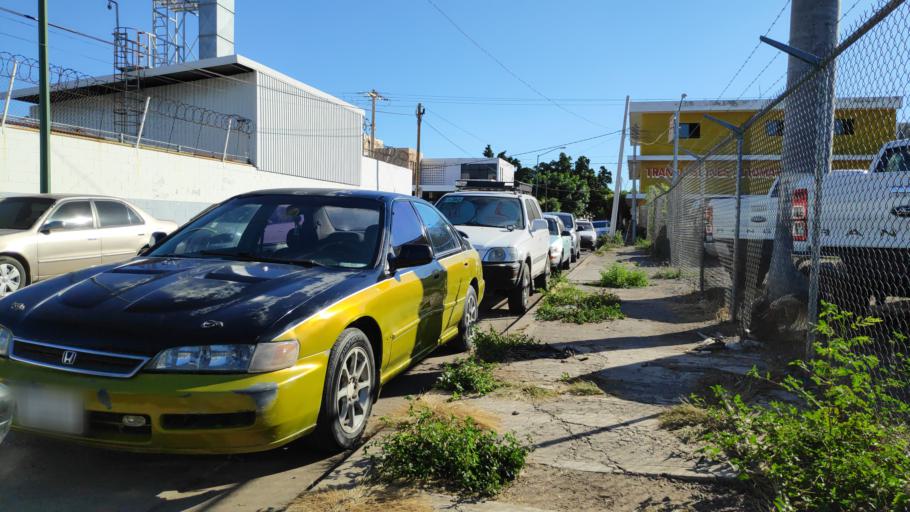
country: MX
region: Sinaloa
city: Culiacan
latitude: 24.7964
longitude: -107.3993
